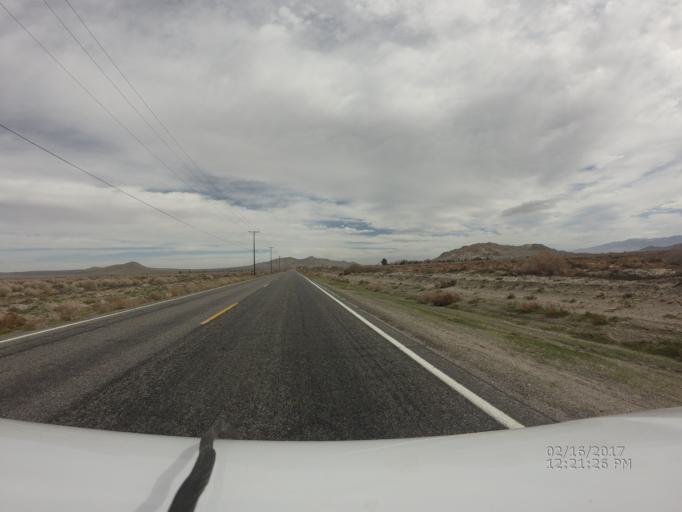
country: US
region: California
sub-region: Los Angeles County
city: Lake Los Angeles
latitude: 34.6754
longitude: -117.8779
